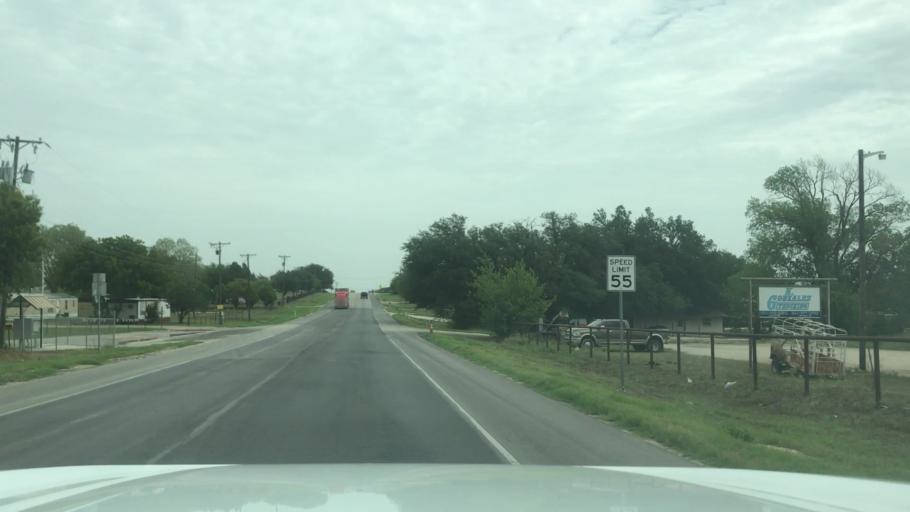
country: US
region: Texas
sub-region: Erath County
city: Dublin
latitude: 32.0838
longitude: -98.3286
